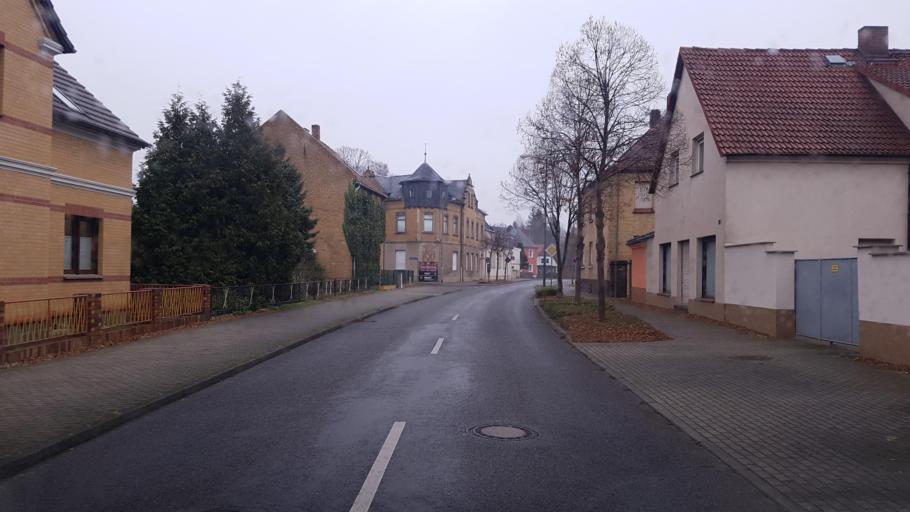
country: DE
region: Brandenburg
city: Lauchhammer
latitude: 51.4928
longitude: 13.7837
